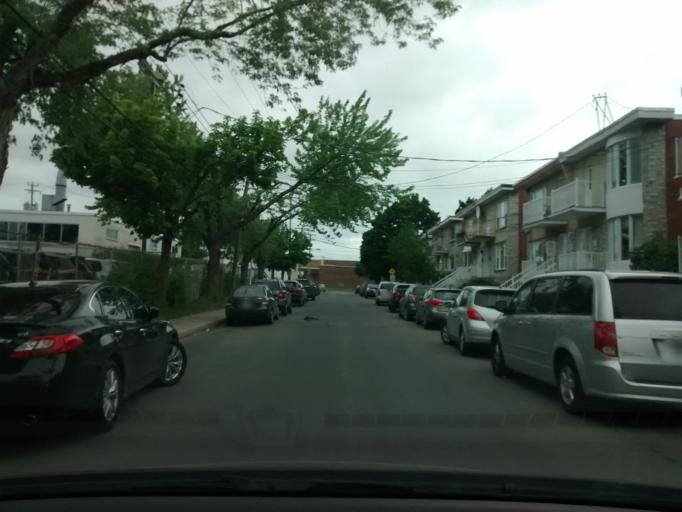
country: CA
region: Quebec
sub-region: Montreal
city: Saint-Leonard
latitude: 45.5869
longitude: -73.6310
